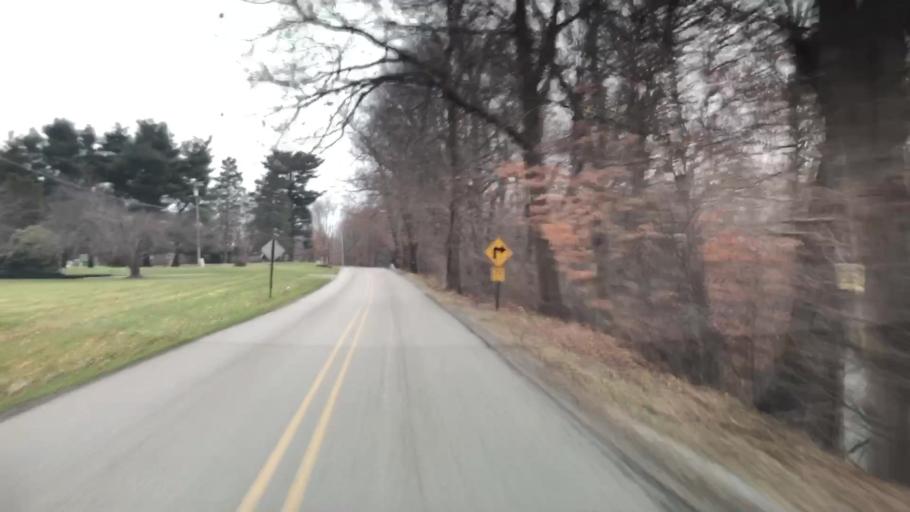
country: US
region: Pennsylvania
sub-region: Mercer County
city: Grove City
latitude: 41.1309
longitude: -80.0907
